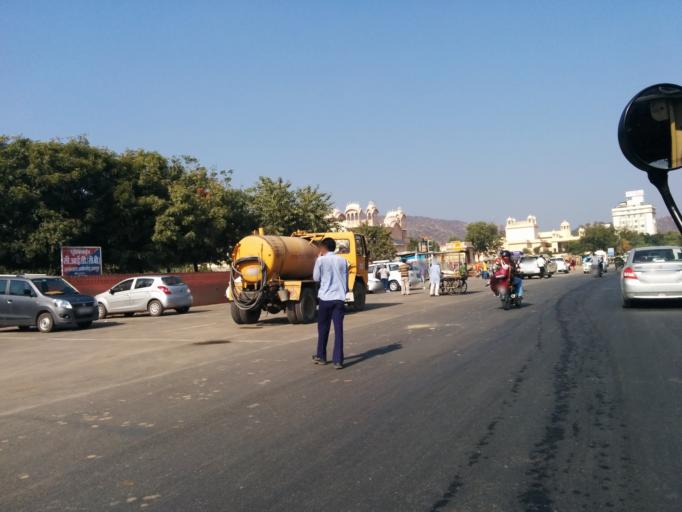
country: IN
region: Rajasthan
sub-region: Jaipur
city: Jaipur
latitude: 26.9547
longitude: 75.8425
